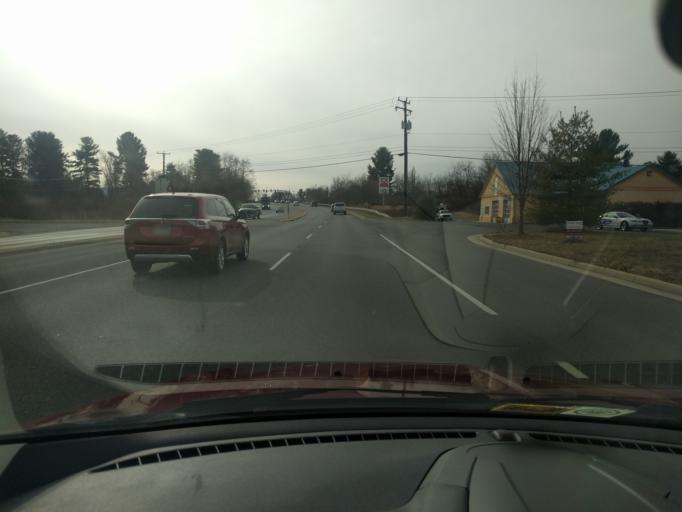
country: US
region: Virginia
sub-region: Augusta County
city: Lyndhurst
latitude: 38.0699
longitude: -78.9372
